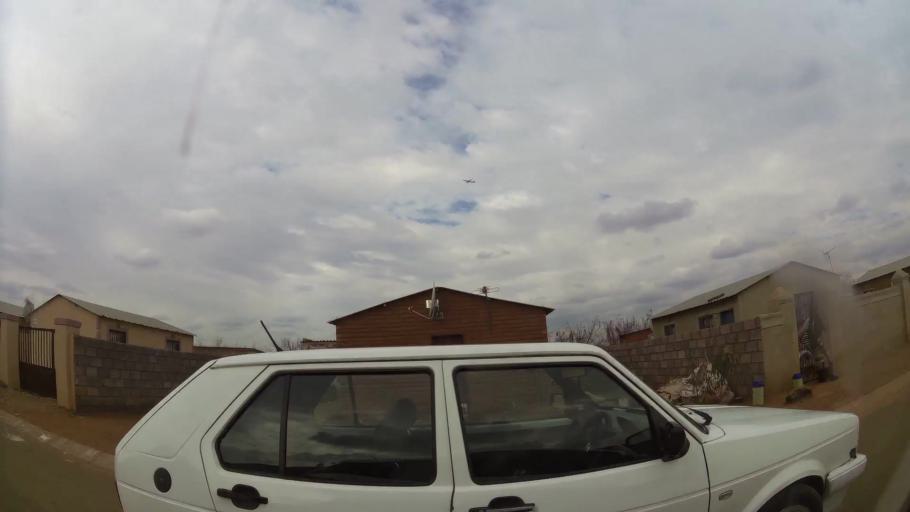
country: ZA
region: Gauteng
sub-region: Ekurhuleni Metropolitan Municipality
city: Germiston
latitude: -26.3898
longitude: 28.1196
